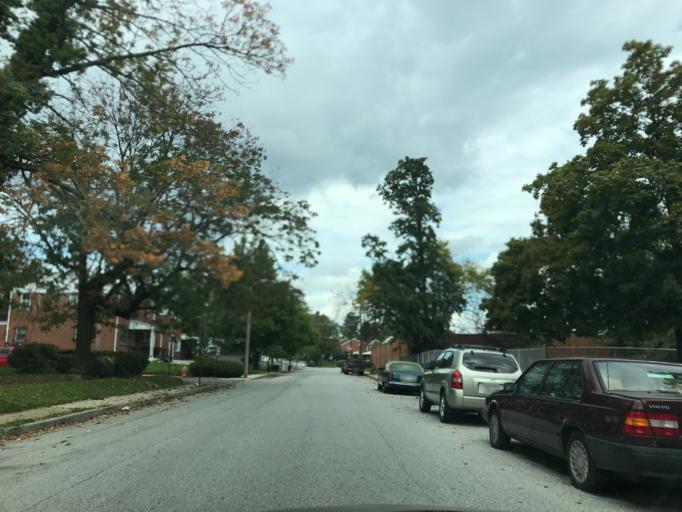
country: US
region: Maryland
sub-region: Baltimore County
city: Lochearn
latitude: 39.3344
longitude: -76.6757
